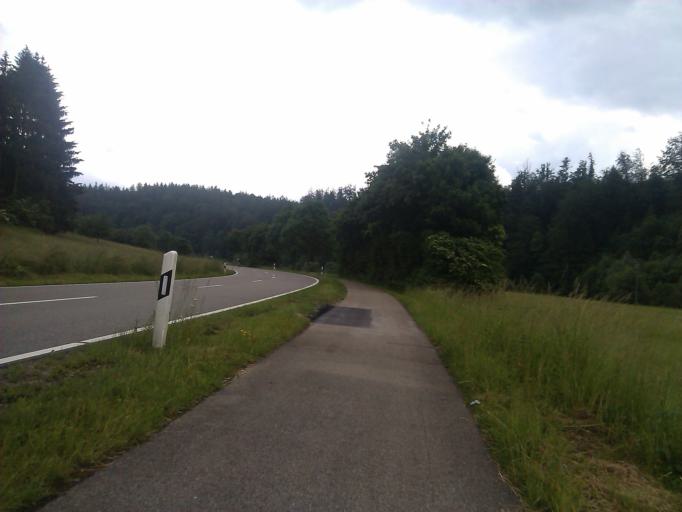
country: DE
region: Baden-Wuerttemberg
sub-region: Regierungsbezirk Stuttgart
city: Abtsgmund
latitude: 48.9044
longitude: 9.9762
